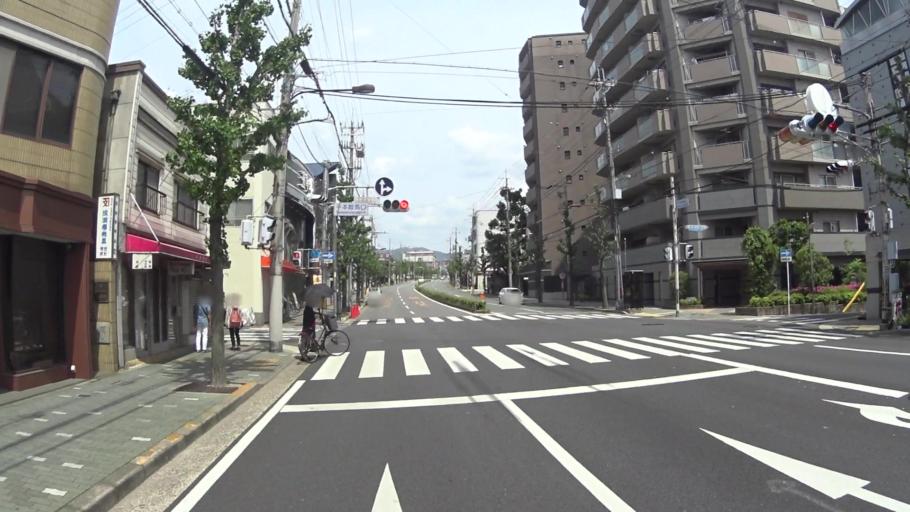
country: JP
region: Kyoto
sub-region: Kyoto-shi
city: Kamigyo-ku
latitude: 35.0358
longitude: 135.7404
